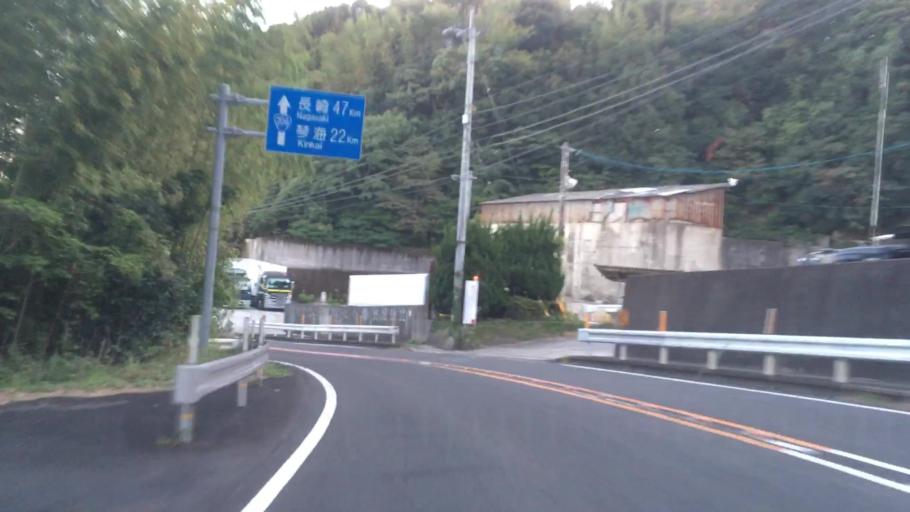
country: JP
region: Nagasaki
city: Sasebo
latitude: 33.0415
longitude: 129.7419
